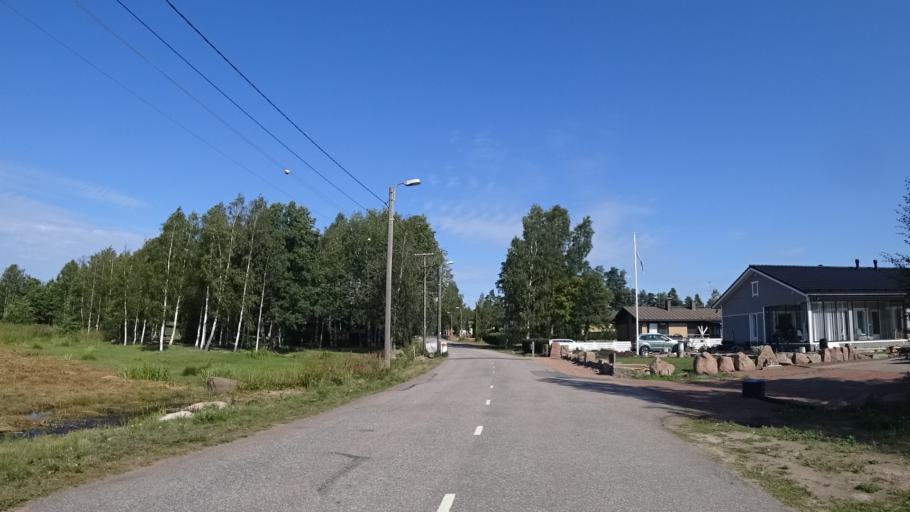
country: FI
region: Kymenlaakso
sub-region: Kotka-Hamina
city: Hamina
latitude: 60.5557
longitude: 27.1999
